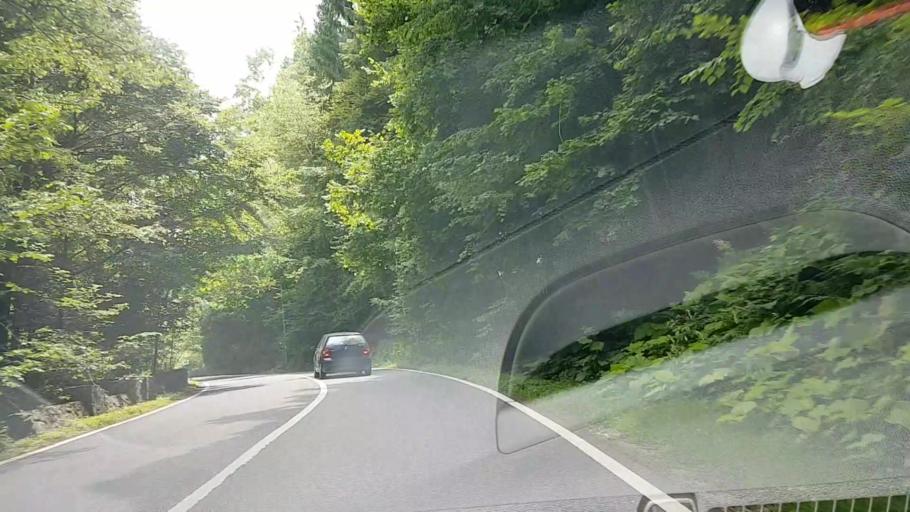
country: RO
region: Suceava
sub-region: Comuna Crucea
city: Crucea
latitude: 47.3044
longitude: 25.6275
